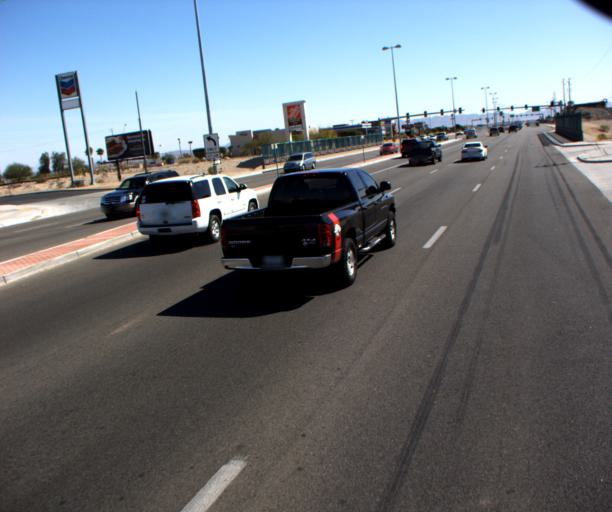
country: US
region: Arizona
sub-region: Yuma County
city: Yuma
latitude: 32.6984
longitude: -114.6130
